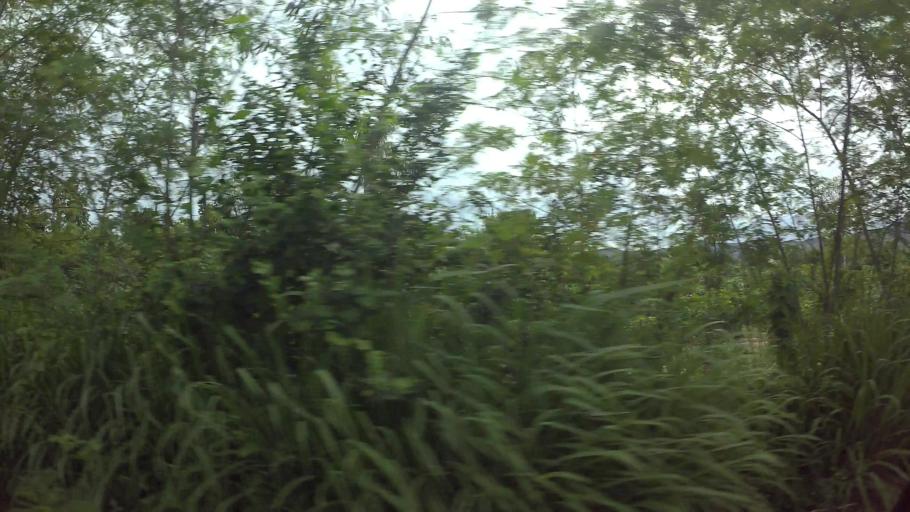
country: TH
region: Chon Buri
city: Sattahip
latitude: 12.7117
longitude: 100.9023
